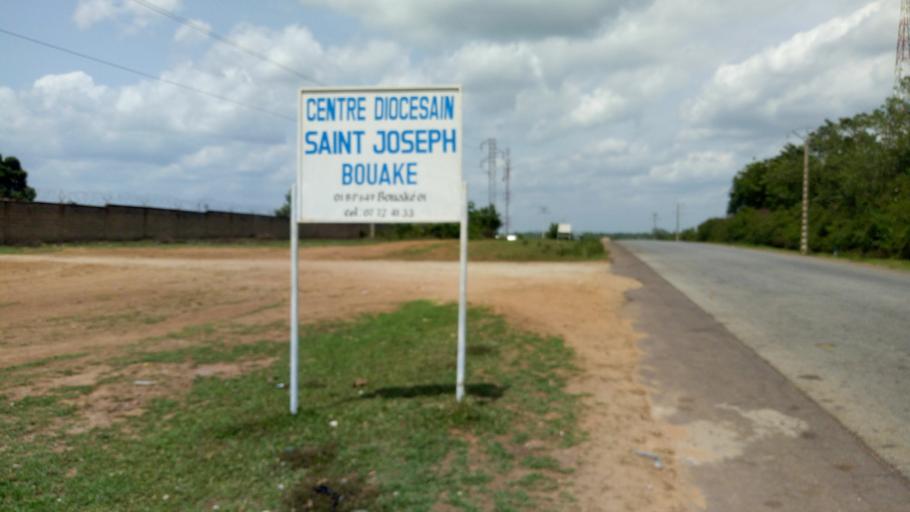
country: CI
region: Vallee du Bandama
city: Bouake
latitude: 7.6974
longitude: -4.9724
